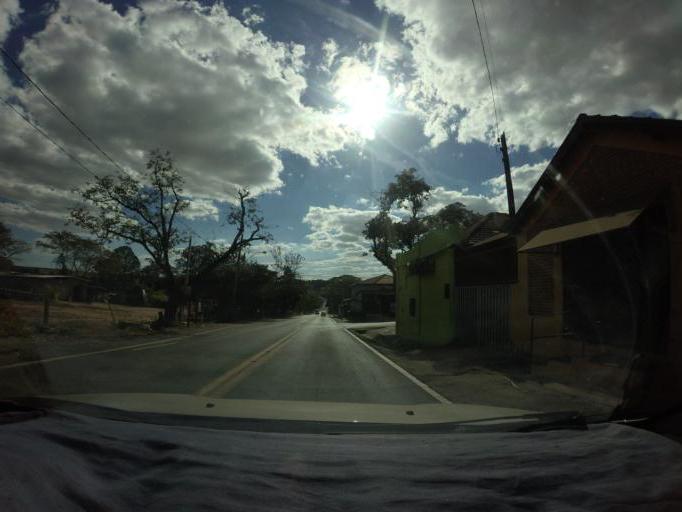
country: BR
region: Sao Paulo
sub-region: Santa Barbara D'Oeste
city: Santa Barbara d'Oeste
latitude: -22.7449
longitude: -47.5274
